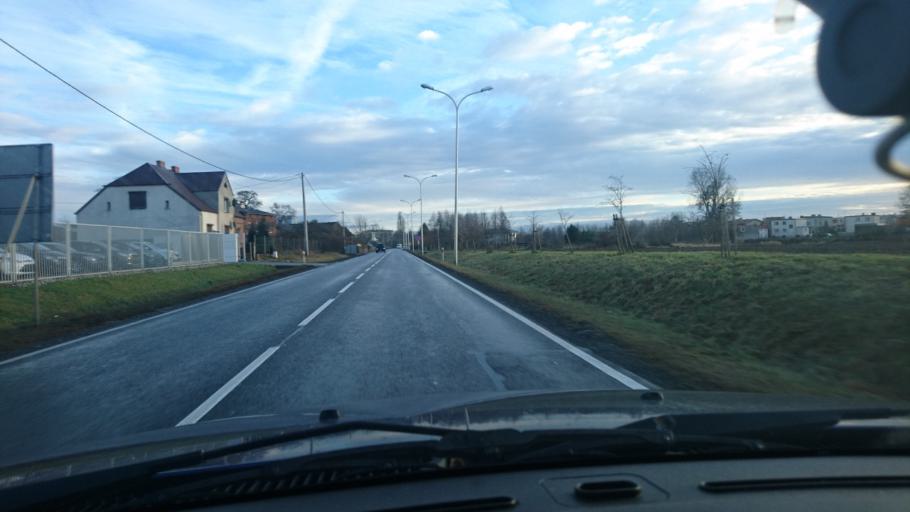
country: PL
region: Greater Poland Voivodeship
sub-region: Powiat kepinski
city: Kepno
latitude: 51.3032
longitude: 17.9923
